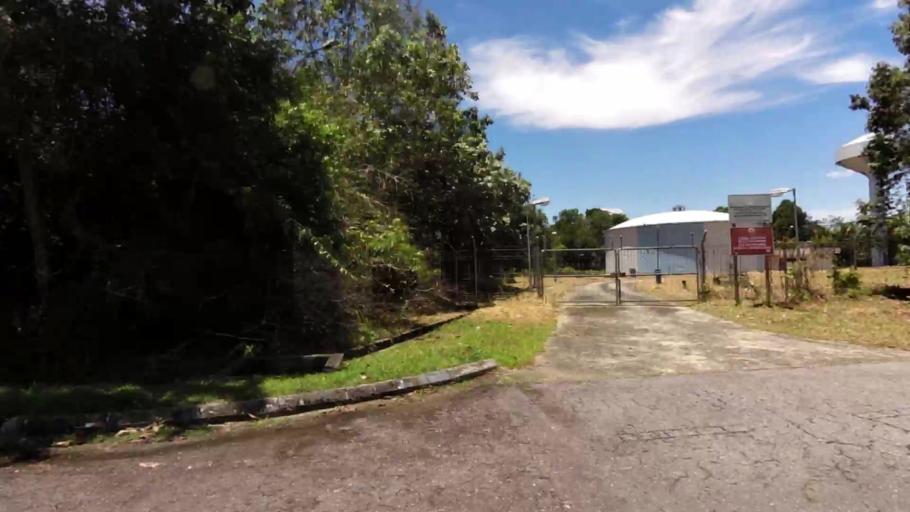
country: BN
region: Brunei and Muara
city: Bandar Seri Begawan
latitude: 4.9209
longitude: 114.9609
